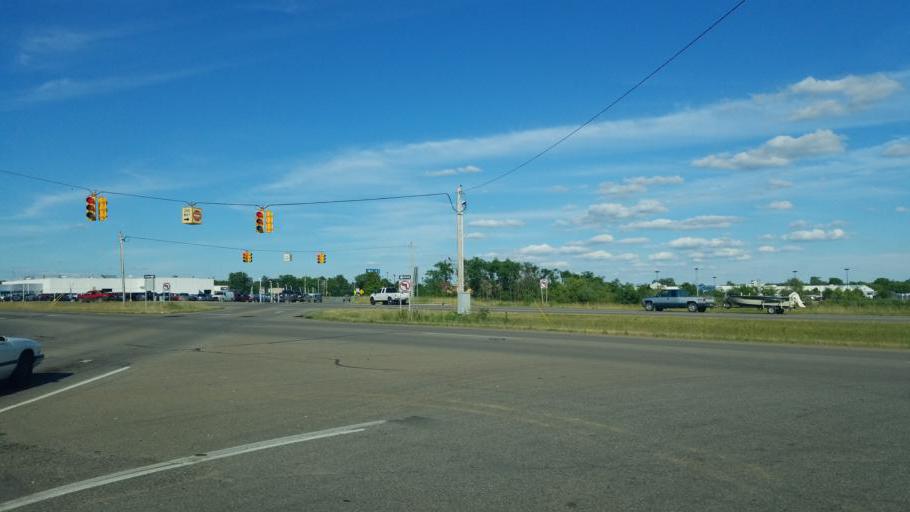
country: US
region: Michigan
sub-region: Eaton County
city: Charlotte
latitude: 42.5821
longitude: -84.8088
